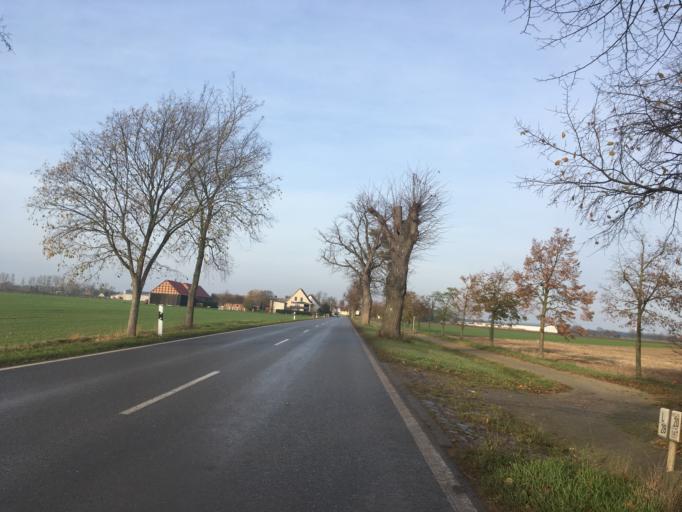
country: DE
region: Brandenburg
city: Wriezen
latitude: 52.7697
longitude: 14.1587
